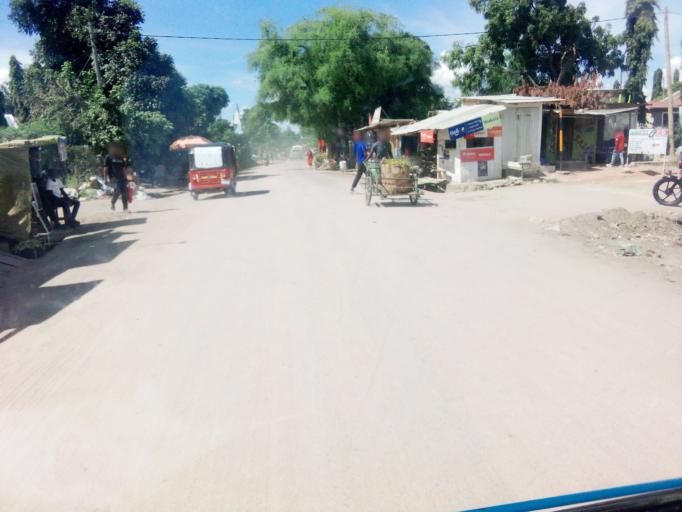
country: TZ
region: Dodoma
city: Dodoma
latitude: -6.1765
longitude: 35.7542
